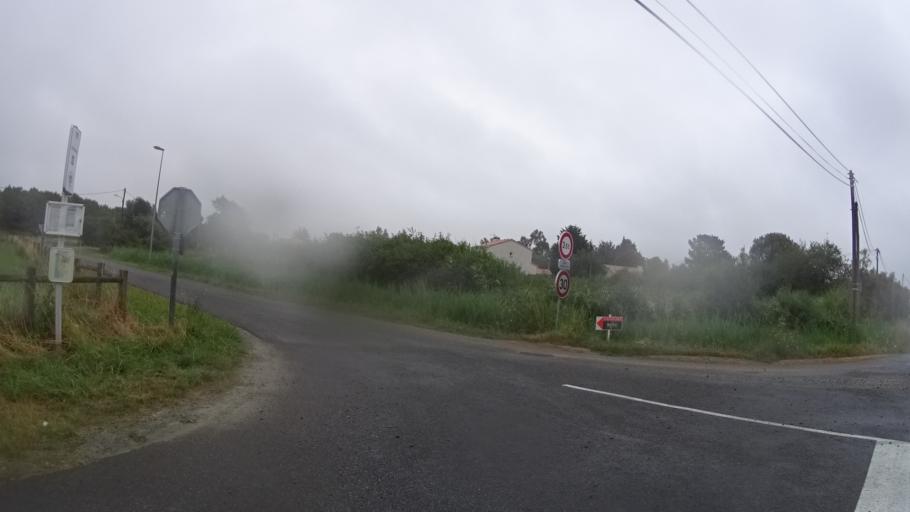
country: FR
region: Pays de la Loire
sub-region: Departement de la Loire-Atlantique
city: Saint-Brevin-les-Pins
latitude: 47.2668
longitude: -2.1498
